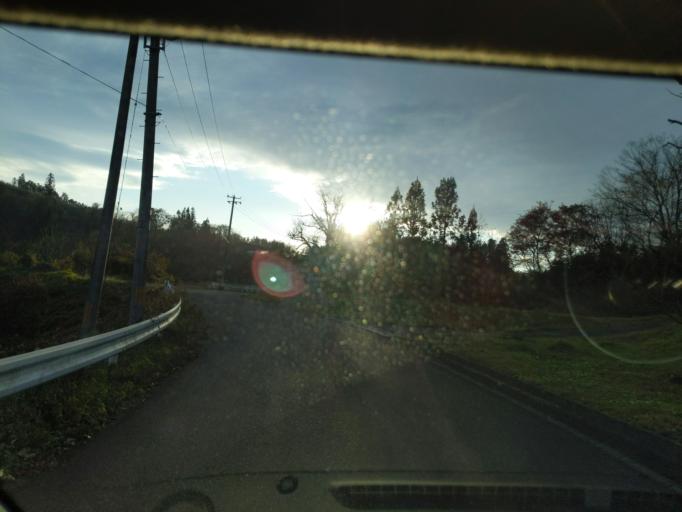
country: JP
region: Iwate
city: Ichinoseki
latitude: 39.0006
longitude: 141.0752
